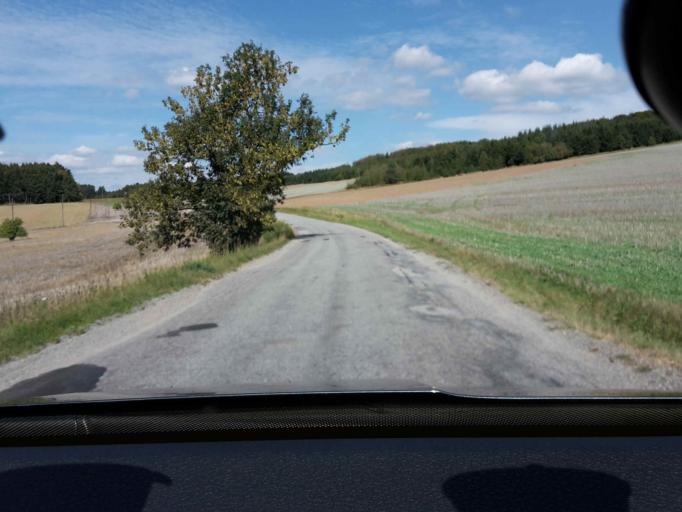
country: CZ
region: Vysocina
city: Zeletava
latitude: 49.1228
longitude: 15.6091
